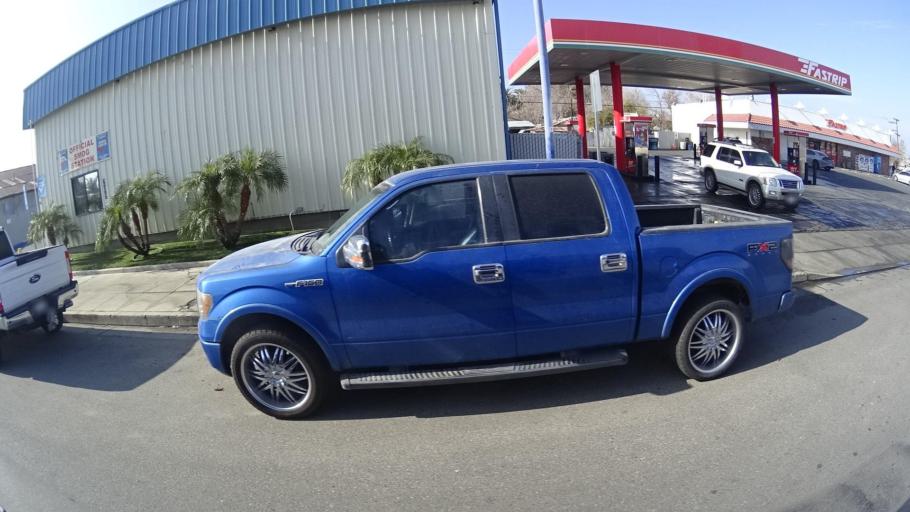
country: US
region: California
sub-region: Kern County
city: Ford City
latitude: 35.1538
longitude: -119.4565
